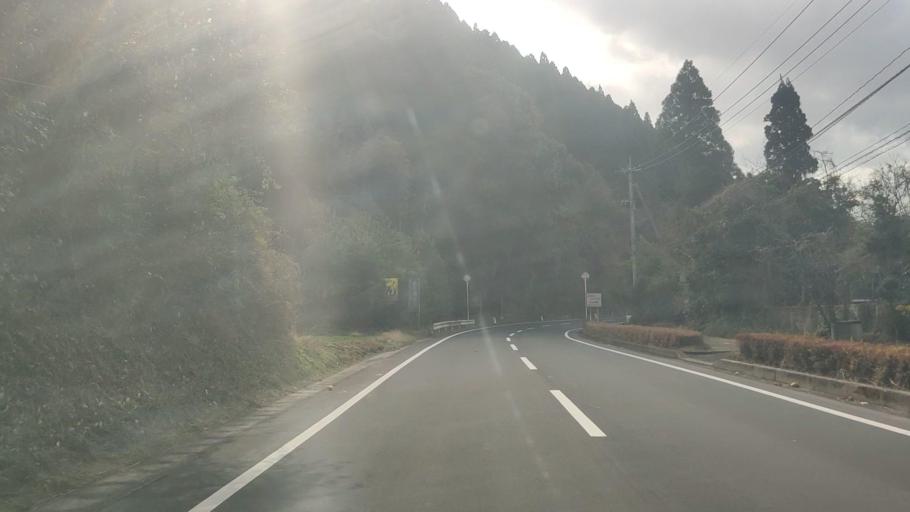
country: JP
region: Kagoshima
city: Okuchi-shinohara
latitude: 31.9613
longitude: 130.7368
